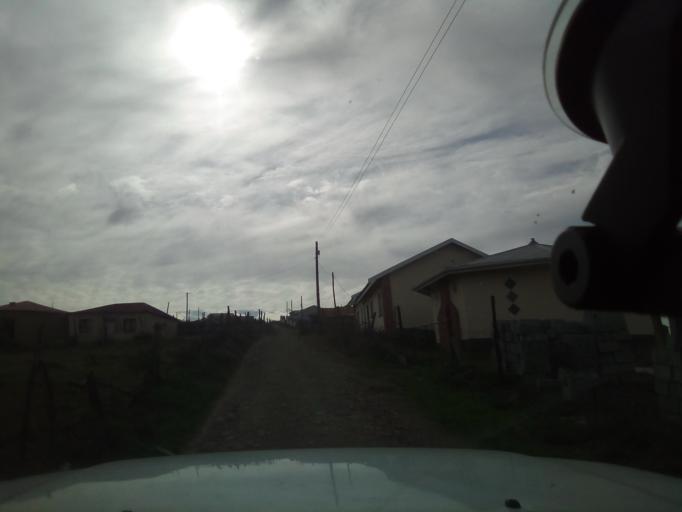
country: ZA
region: Eastern Cape
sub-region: Buffalo City Metropolitan Municipality
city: East London
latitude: -32.7965
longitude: 27.9675
